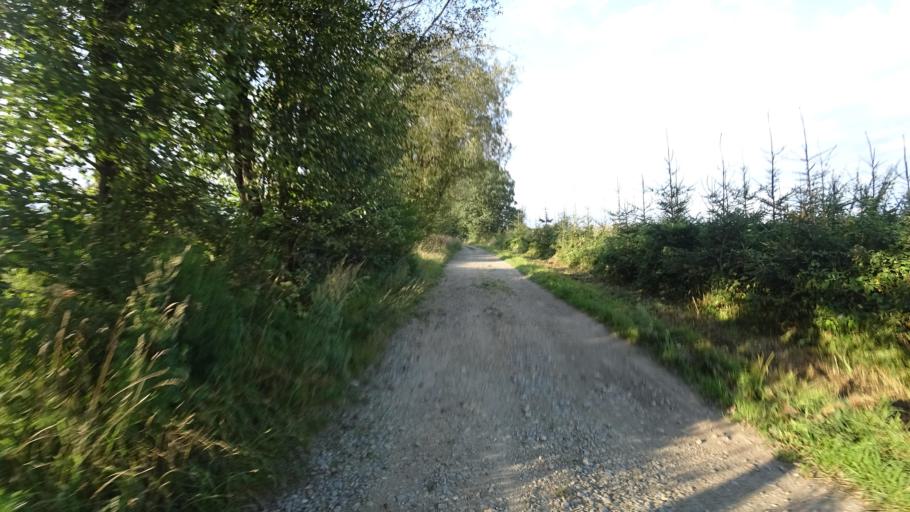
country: BE
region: Wallonia
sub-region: Province du Luxembourg
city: Neufchateau
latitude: 49.8684
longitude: 5.3744
